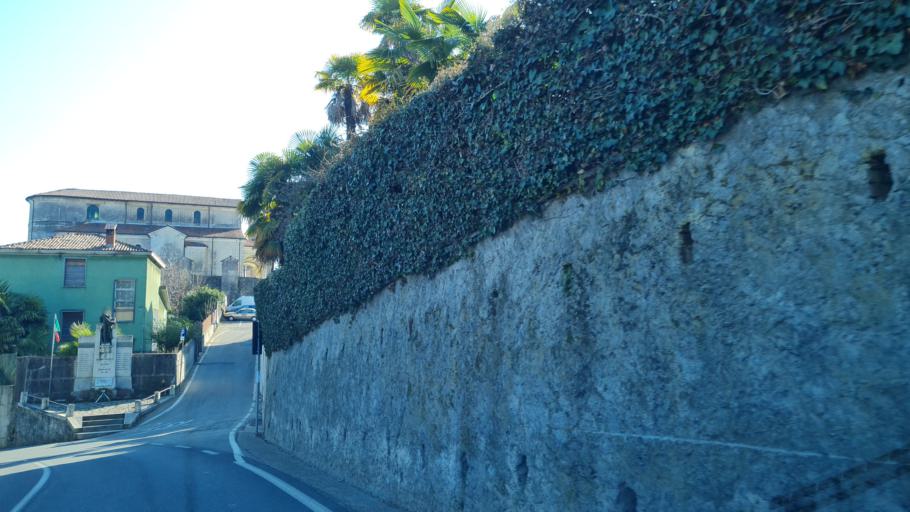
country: IT
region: Piedmont
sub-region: Provincia di Novara
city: Meina
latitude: 45.7810
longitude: 8.5362
